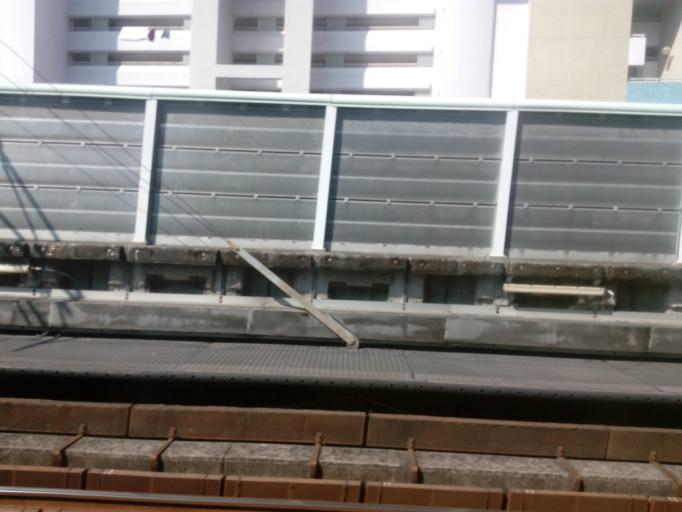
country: HK
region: Sai Kung
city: Sai Kung
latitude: 22.4228
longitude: 114.2277
